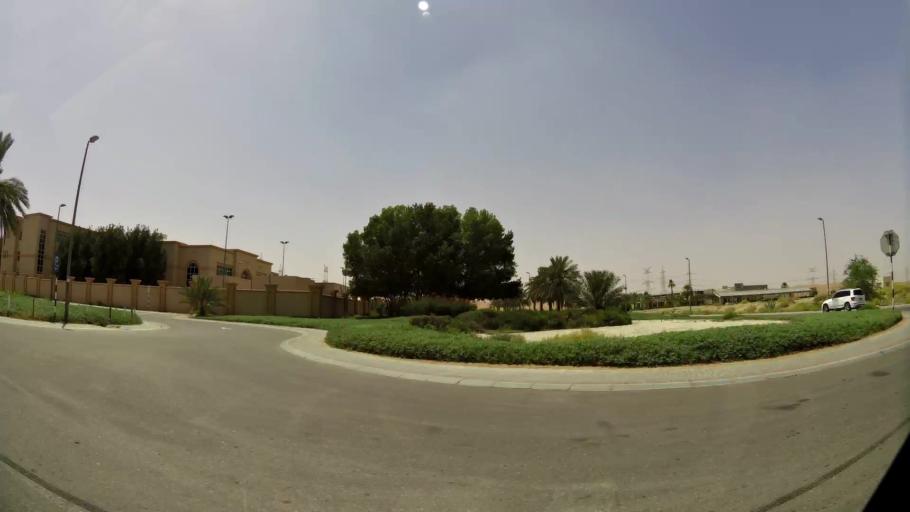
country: AE
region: Abu Dhabi
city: Al Ain
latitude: 24.2592
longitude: 55.6935
